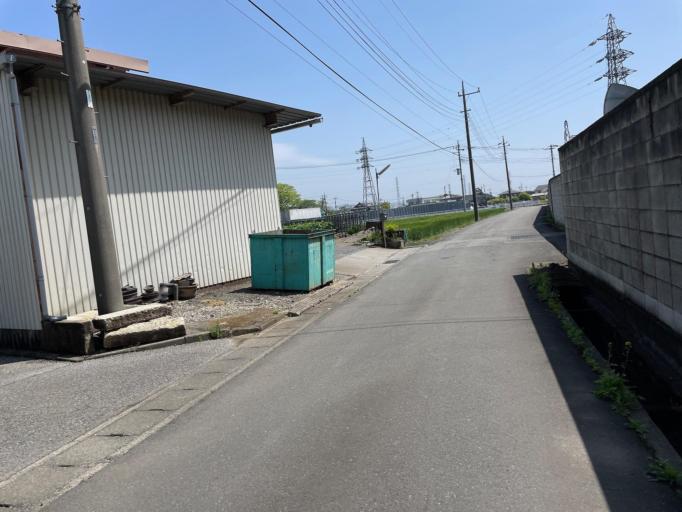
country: JP
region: Tochigi
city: Ashikaga
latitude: 36.3037
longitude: 139.4253
